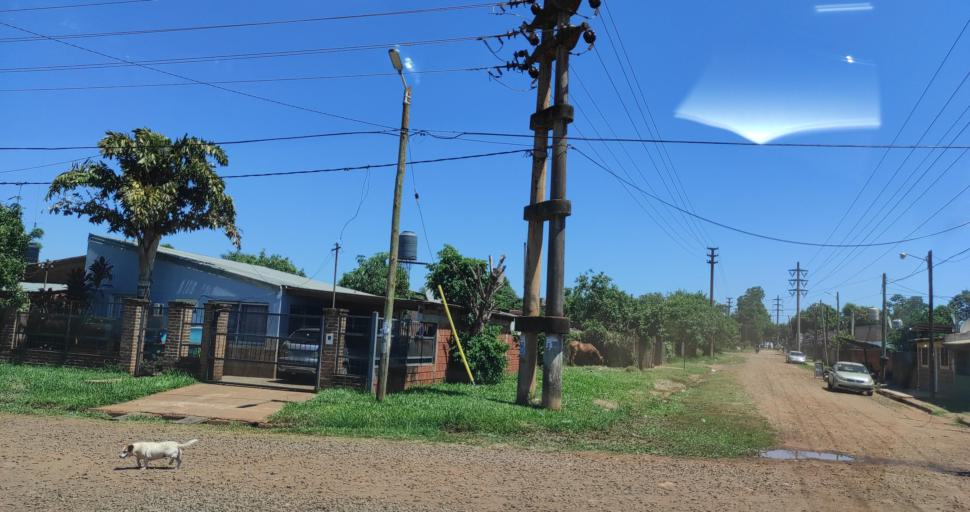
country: AR
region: Misiones
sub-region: Departamento de Capital
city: Posadas
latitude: -27.4135
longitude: -55.9083
